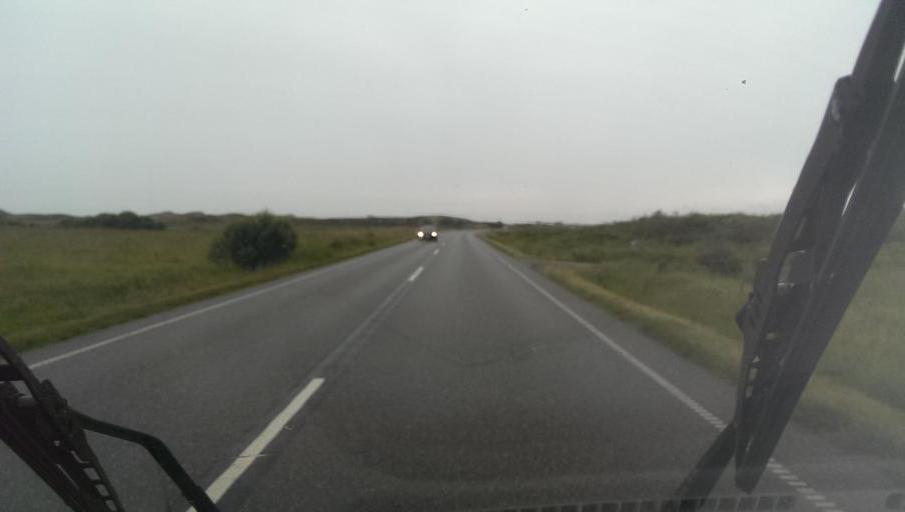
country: DK
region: Central Jutland
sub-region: Ringkobing-Skjern Kommune
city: Hvide Sande
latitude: 55.8913
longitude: 8.1722
